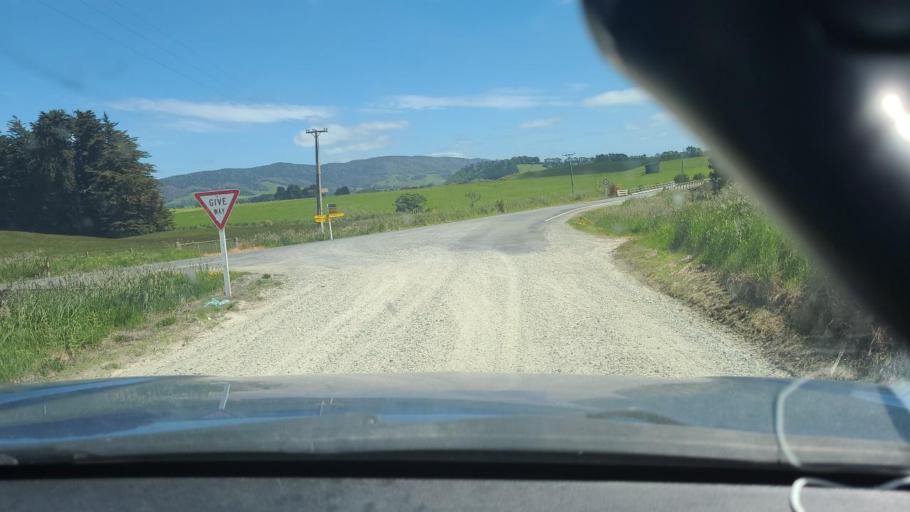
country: NZ
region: Southland
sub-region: Gore District
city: Gore
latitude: -46.4159
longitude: 169.0676
